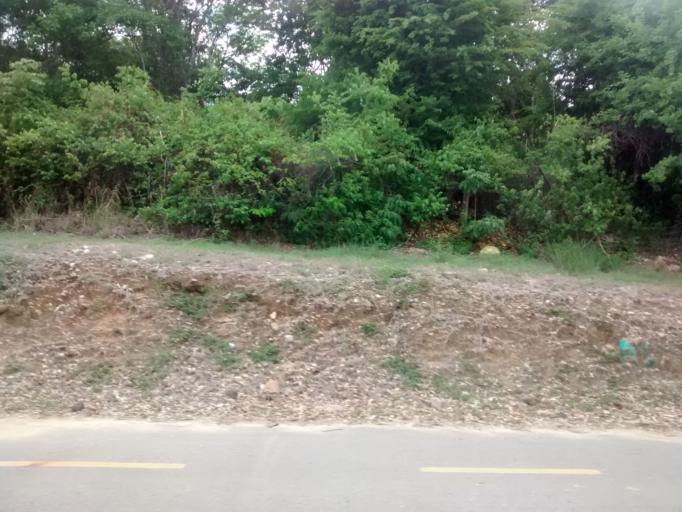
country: CO
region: Cundinamarca
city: Ricaurte
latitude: 4.2750
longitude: -74.7577
